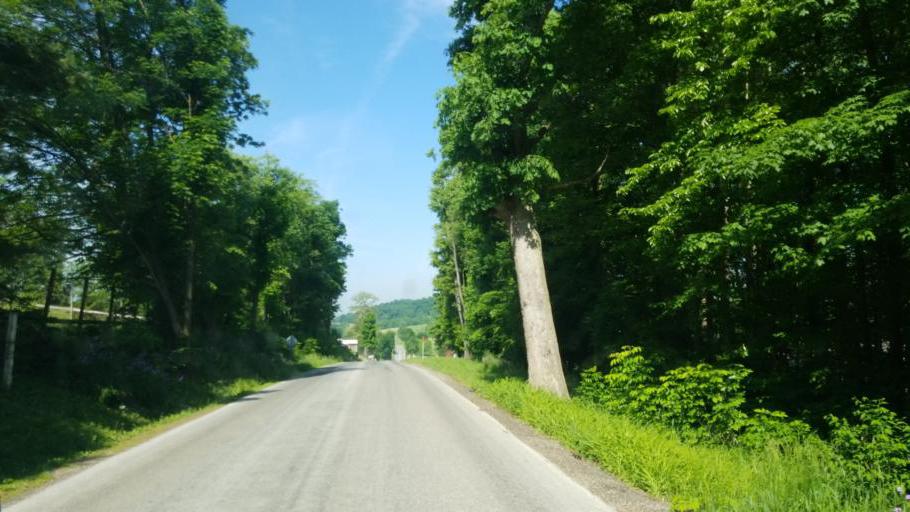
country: US
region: Ohio
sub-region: Tuscarawas County
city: Sugarcreek
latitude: 40.4463
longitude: -81.7799
